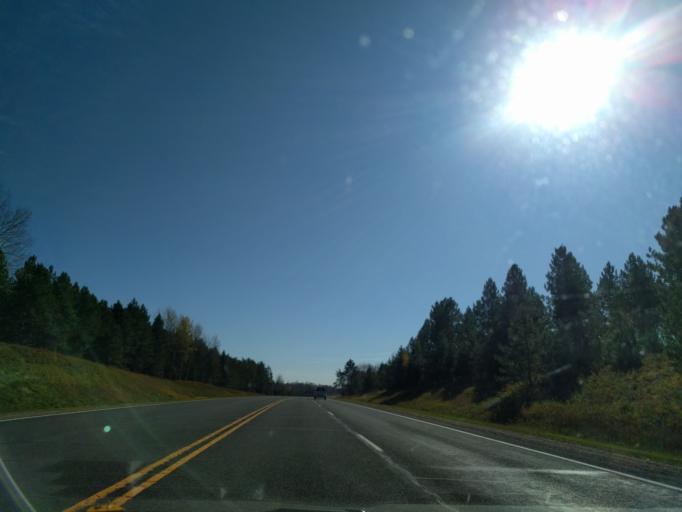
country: US
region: Michigan
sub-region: Iron County
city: Crystal Falls
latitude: 46.2419
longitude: -88.0088
